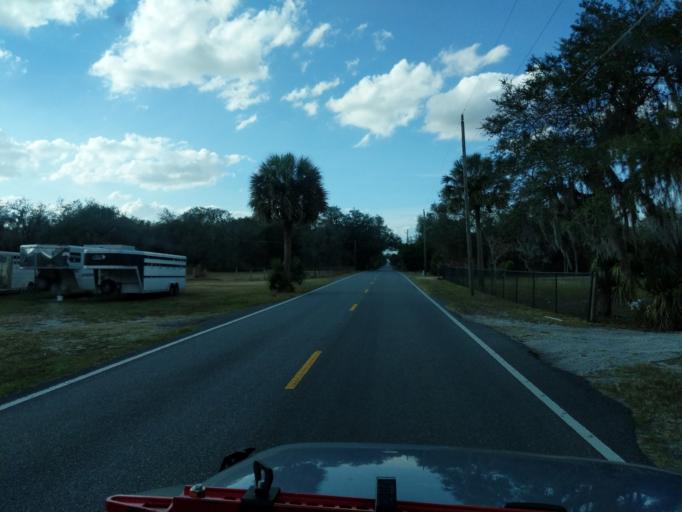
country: US
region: Florida
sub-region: Seminole County
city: Geneva
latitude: 28.7597
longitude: -81.1287
